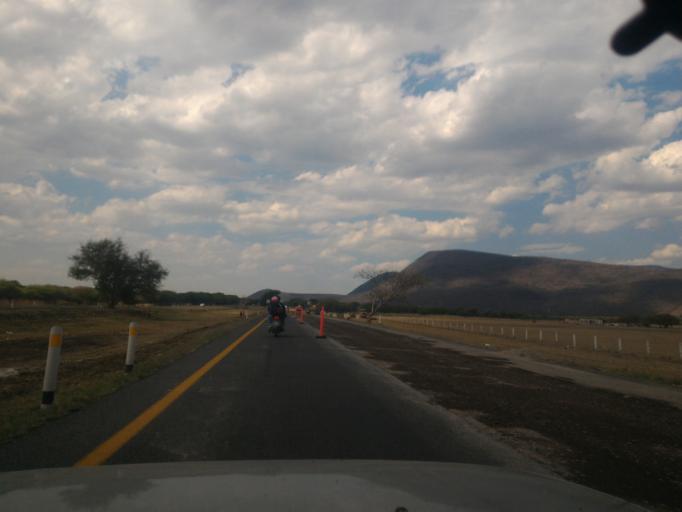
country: MX
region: Jalisco
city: Zacoalco de Torres
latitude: 20.1637
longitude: -103.5023
